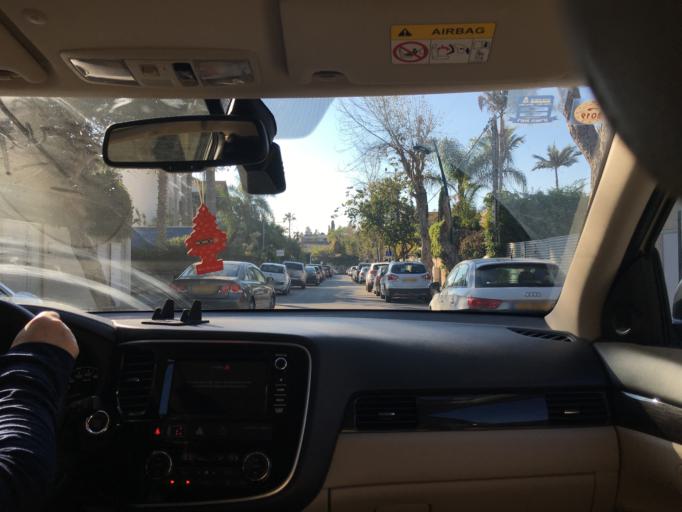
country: IL
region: Tel Aviv
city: Ramat HaSharon
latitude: 32.1519
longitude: 34.8312
